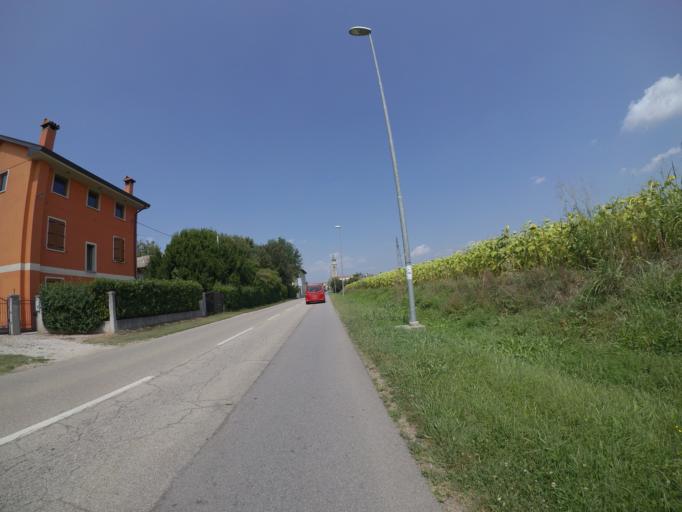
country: IT
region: Friuli Venezia Giulia
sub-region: Provincia di Udine
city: Codroipo
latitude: 45.9830
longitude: 12.9708
